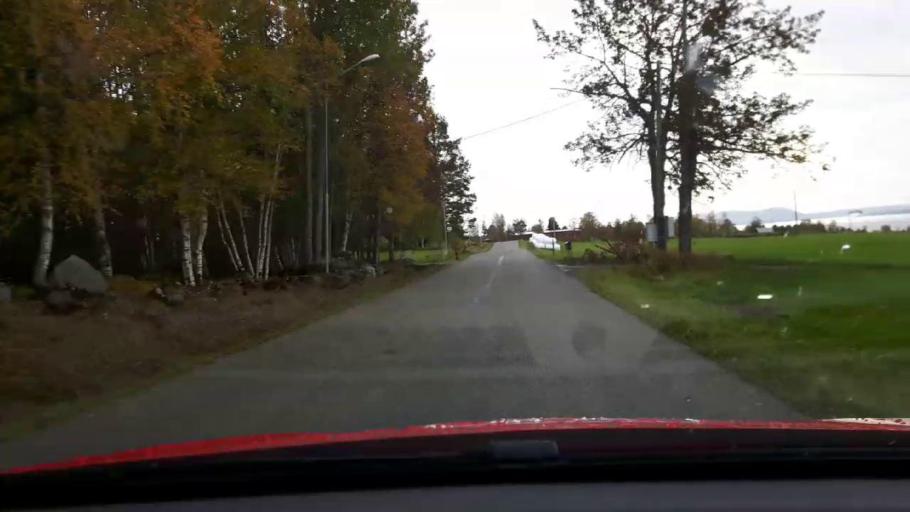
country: SE
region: Jaemtland
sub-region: Bergs Kommun
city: Hoverberg
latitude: 62.9510
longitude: 14.4909
